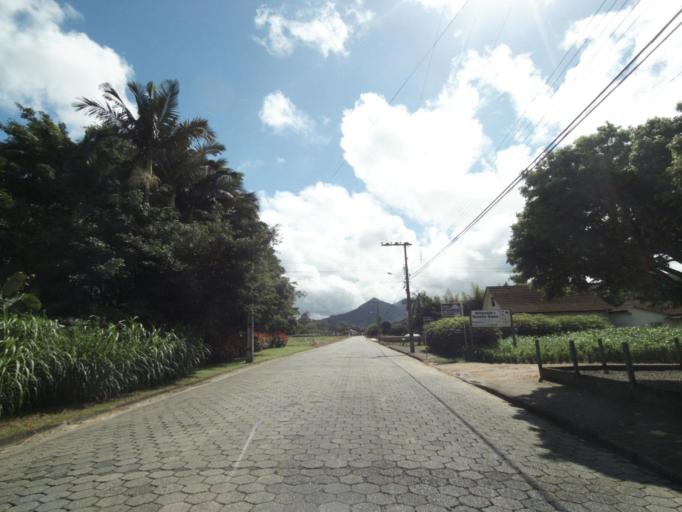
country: BR
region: Santa Catarina
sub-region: Pomerode
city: Pomerode
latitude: -26.6960
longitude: -49.1735
